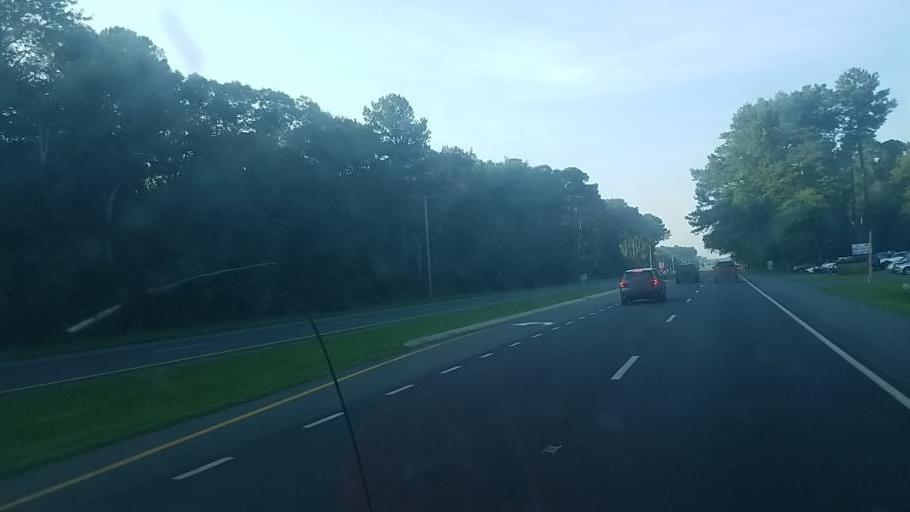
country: US
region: Delaware
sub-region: Sussex County
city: Selbyville
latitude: 38.4728
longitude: -75.2349
